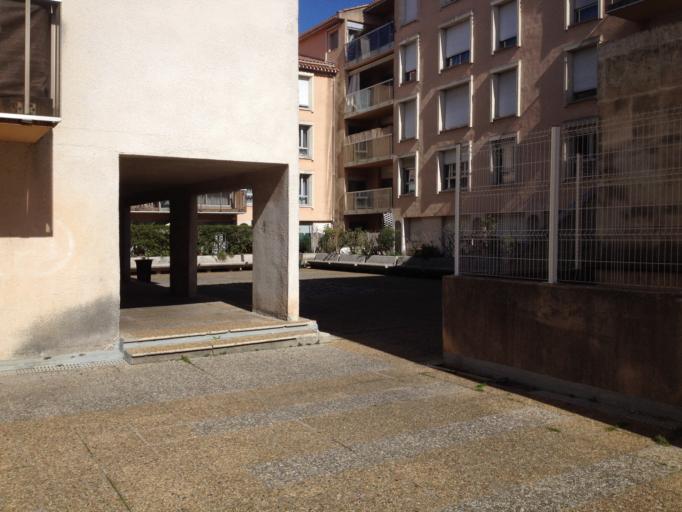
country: FR
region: Provence-Alpes-Cote d'Azur
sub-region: Departement du Vaucluse
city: Avignon
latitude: 43.9515
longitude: 4.8052
